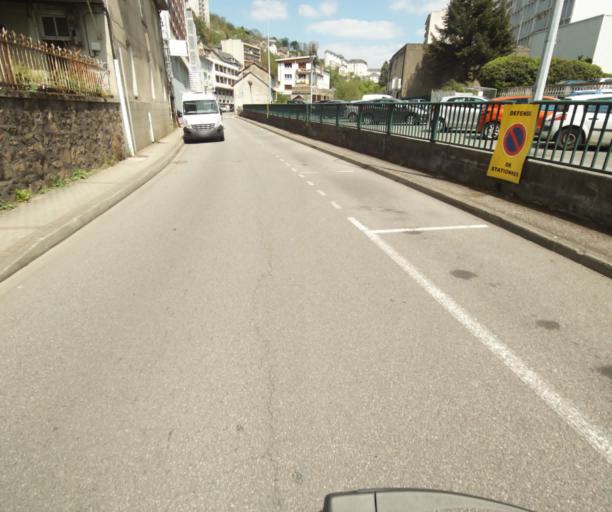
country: FR
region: Limousin
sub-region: Departement de la Correze
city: Tulle
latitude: 45.2625
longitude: 1.7598
